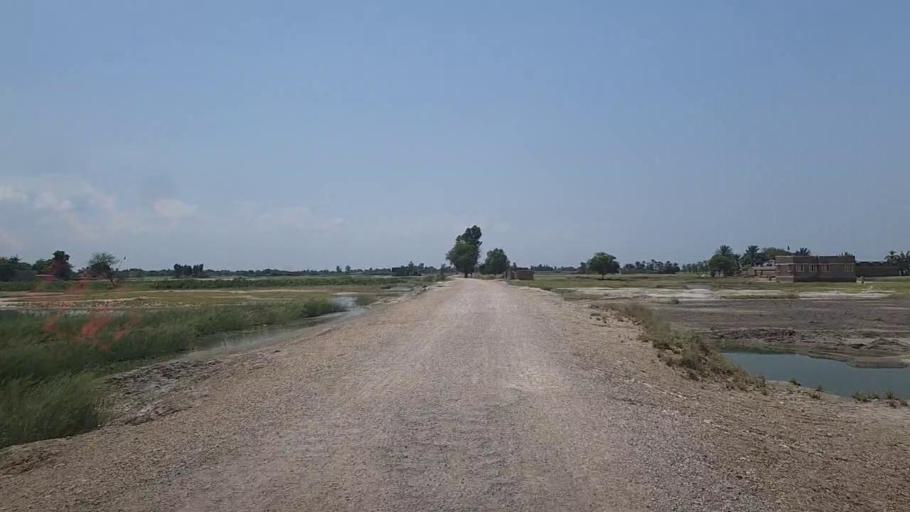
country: PK
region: Sindh
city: Ubauro
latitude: 28.1626
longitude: 69.7645
